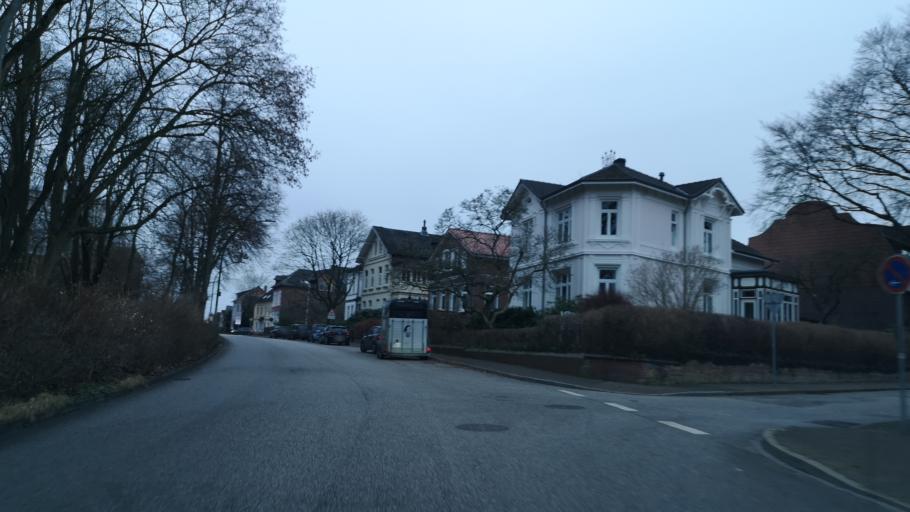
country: DE
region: Schleswig-Holstein
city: Itzehoe
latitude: 53.9189
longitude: 9.5274
